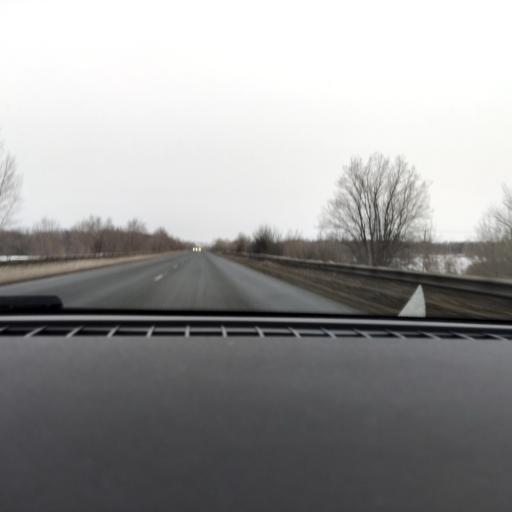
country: RU
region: Samara
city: Kinel'
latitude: 53.1996
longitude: 50.5107
